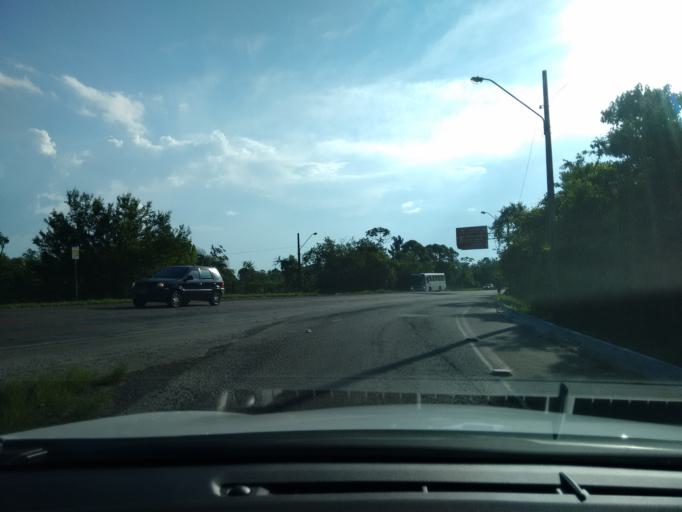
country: BR
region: Santa Catarina
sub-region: Blumenau
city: Blumenau
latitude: -26.8614
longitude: -49.0814
